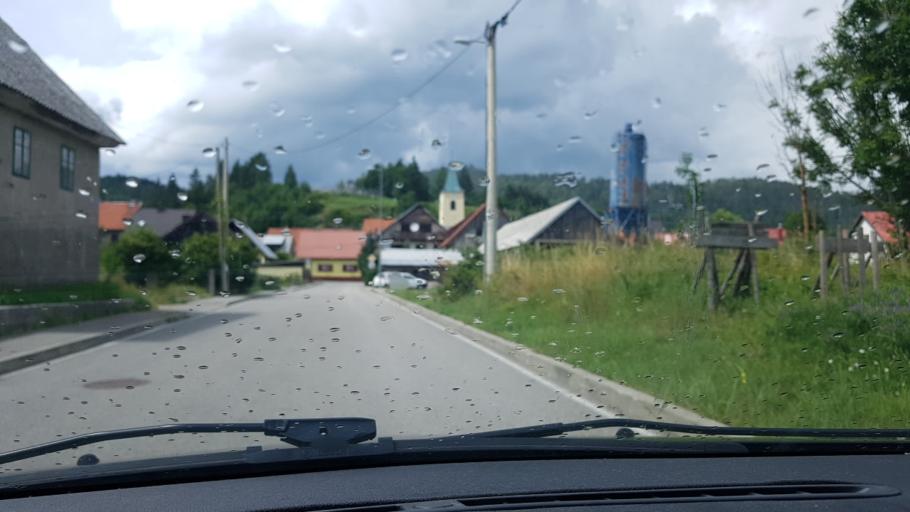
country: HR
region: Primorsko-Goranska
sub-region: Grad Delnice
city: Delnice
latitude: 45.3568
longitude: 14.7518
